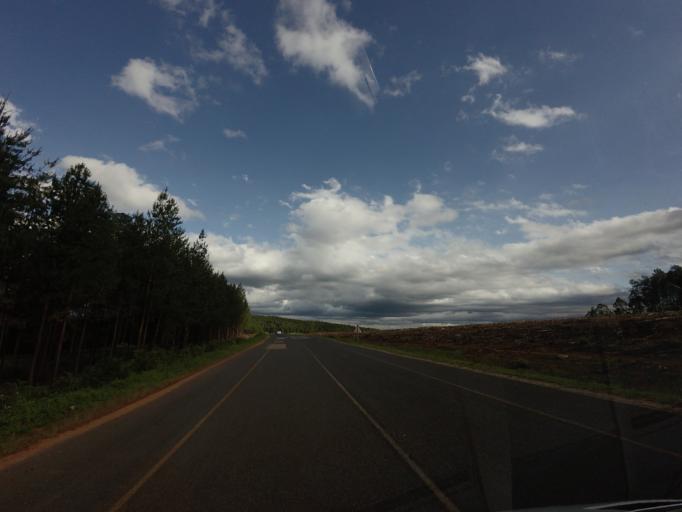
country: ZA
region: Mpumalanga
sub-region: Ehlanzeni District
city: Graksop
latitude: -24.9774
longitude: 30.9474
